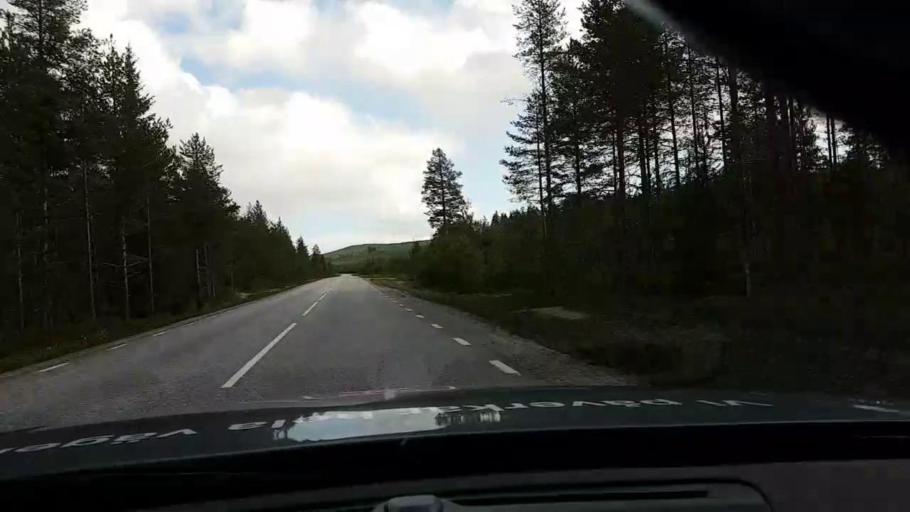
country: SE
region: Vaesternorrland
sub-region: OErnskoeldsviks Kommun
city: Bredbyn
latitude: 63.6841
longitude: 17.7779
